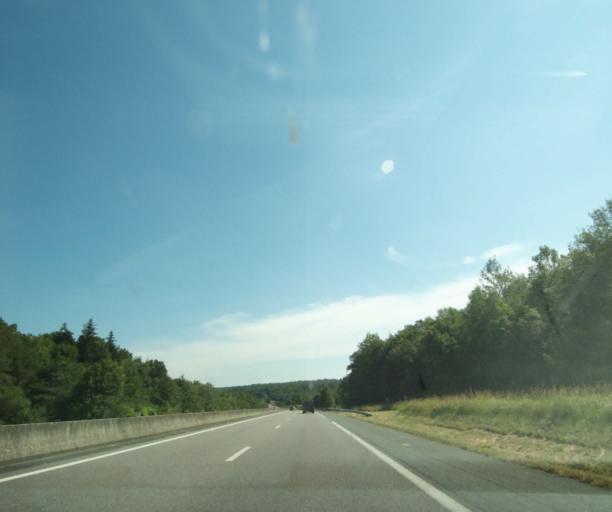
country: FR
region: Lorraine
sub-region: Departement de Meurthe-et-Moselle
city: Colombey-les-Belles
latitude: 48.4795
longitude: 5.8930
